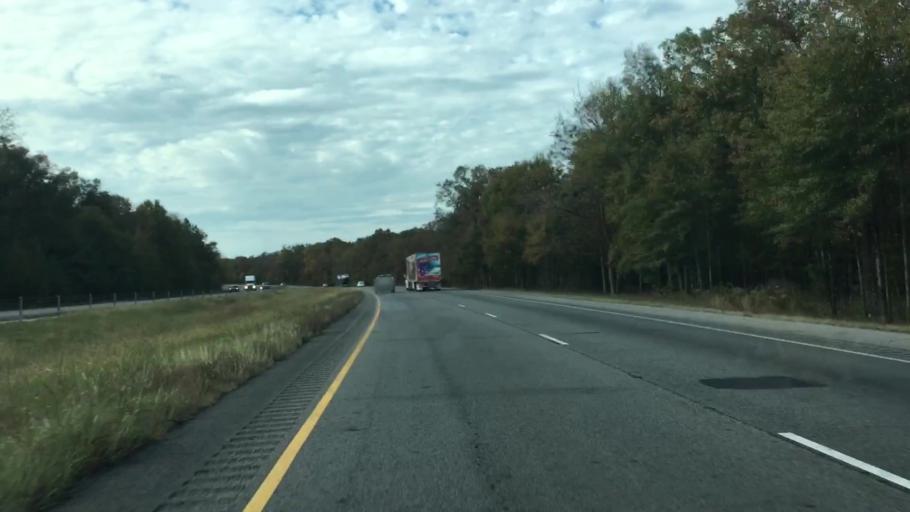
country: US
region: Arkansas
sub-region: Pope County
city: Atkins
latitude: 35.2441
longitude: -92.8630
